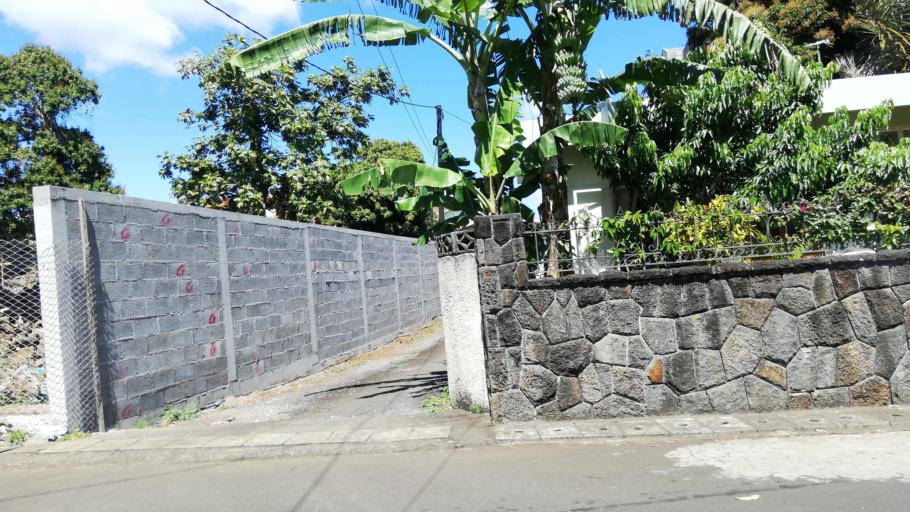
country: MU
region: Moka
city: Moka
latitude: -20.2271
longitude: 57.4711
